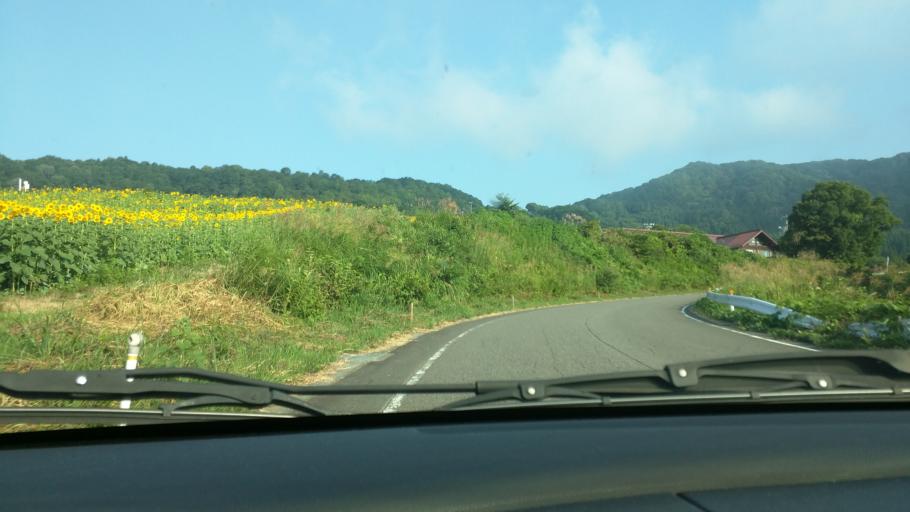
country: JP
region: Fukushima
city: Kitakata
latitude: 37.7479
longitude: 139.8680
